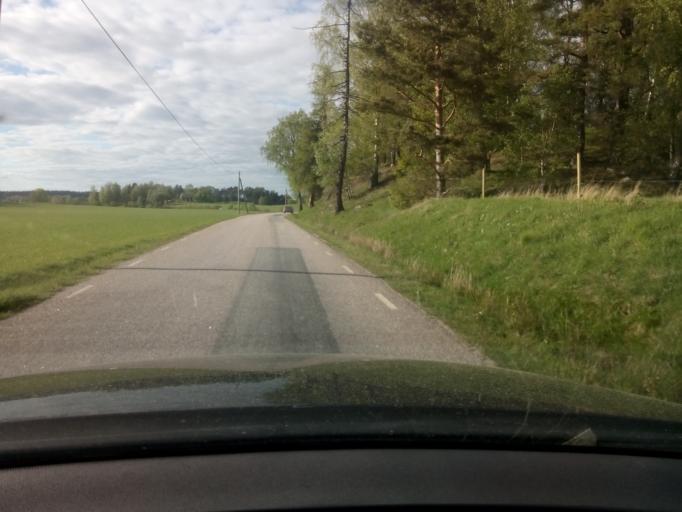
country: SE
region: Soedermanland
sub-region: Nykopings Kommun
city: Stigtomta
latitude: 58.9166
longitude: 16.8794
